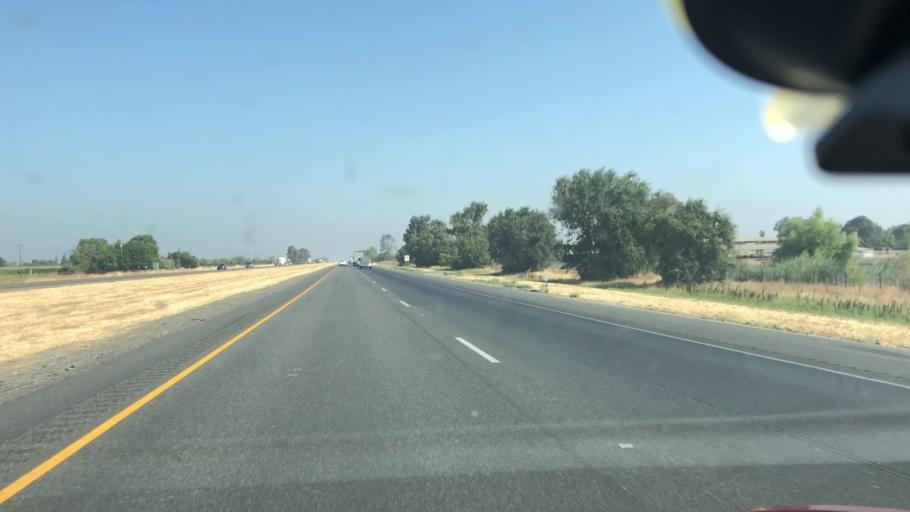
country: US
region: California
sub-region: Sacramento County
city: Walnut Grove
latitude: 38.3252
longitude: -121.4662
